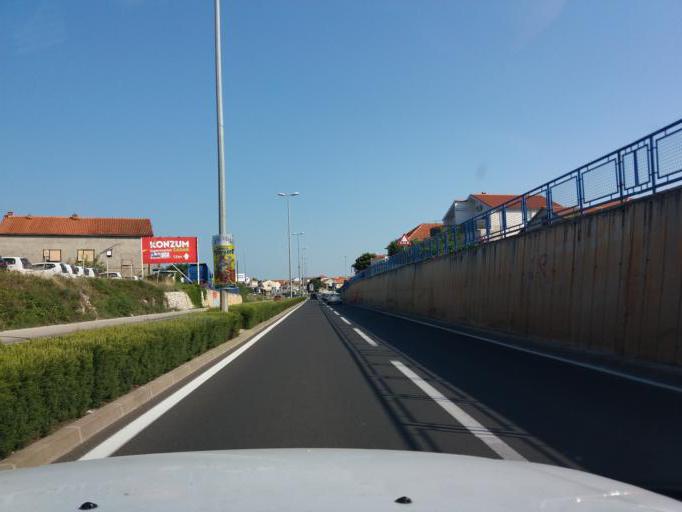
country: HR
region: Zadarska
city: Zadar
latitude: 44.1064
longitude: 15.2619
